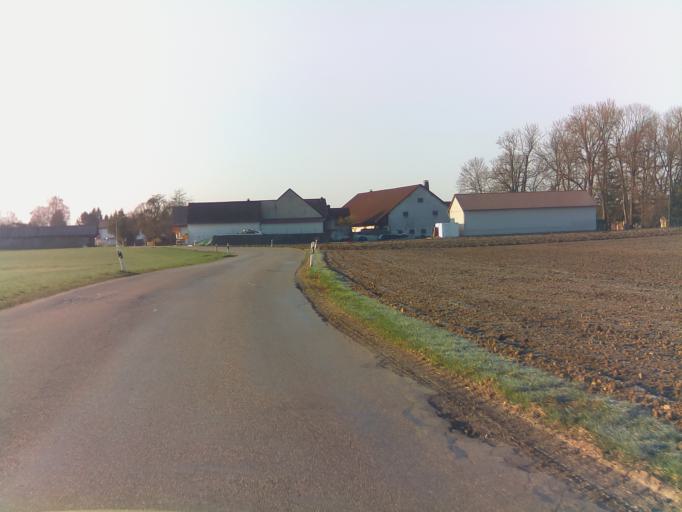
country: DE
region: Bavaria
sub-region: Upper Bavaria
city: Geltendorf
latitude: 48.1472
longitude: 11.0169
